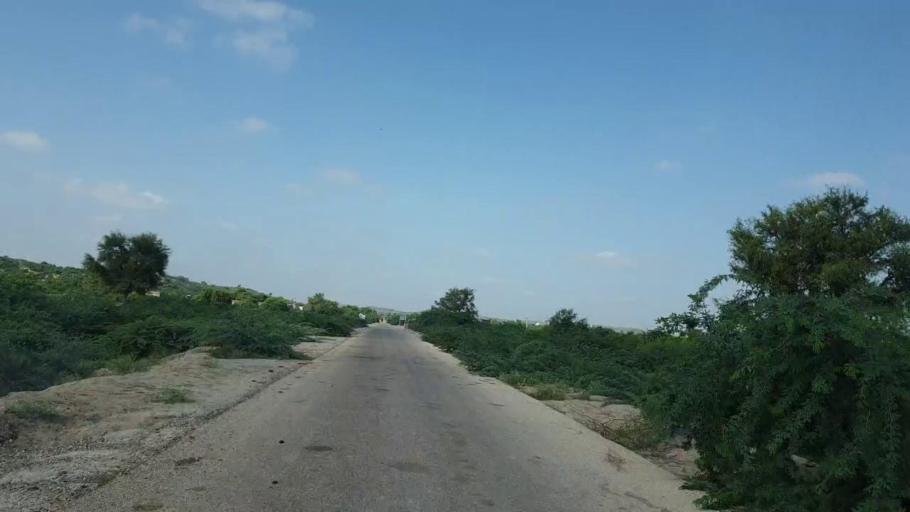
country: PK
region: Sindh
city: Mithi
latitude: 24.5332
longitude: 69.8471
